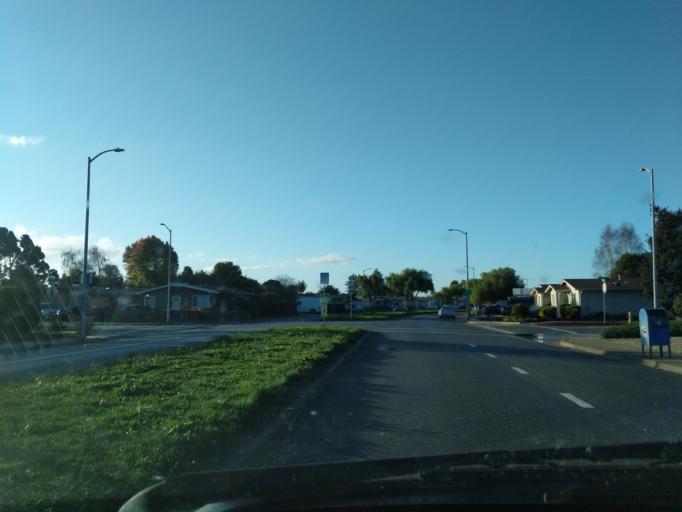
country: US
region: California
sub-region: Monterey County
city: Pajaro
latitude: 36.9199
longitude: -121.7405
